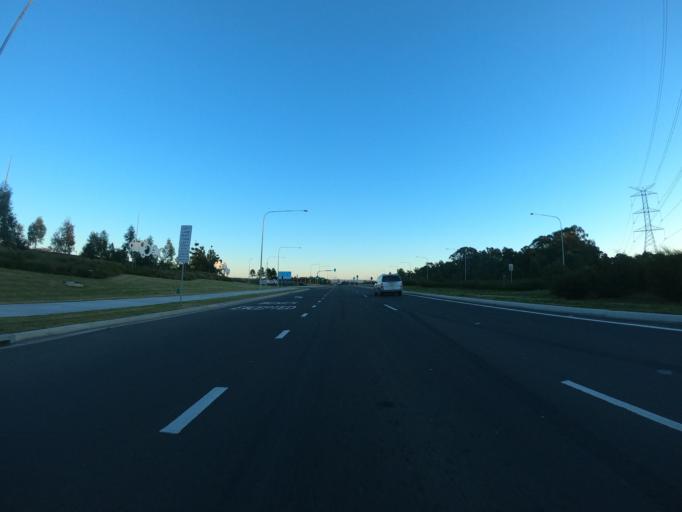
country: AU
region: New South Wales
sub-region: Blacktown
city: Riverstone
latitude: -33.6924
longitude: 150.8268
